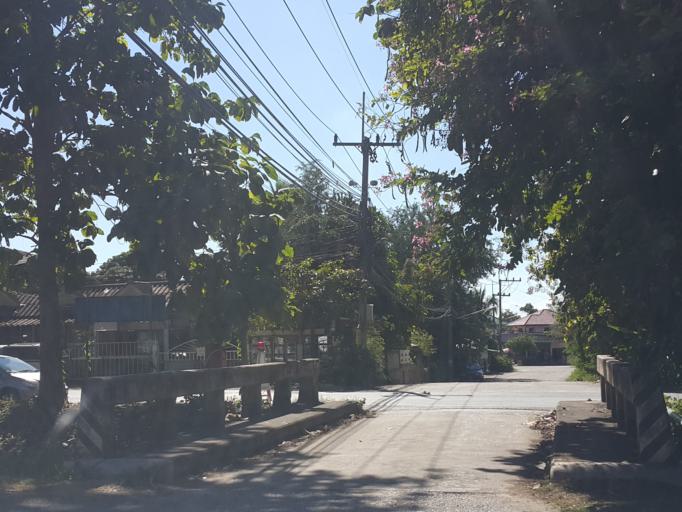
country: TH
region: Chiang Mai
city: San Sai
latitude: 18.8821
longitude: 99.1421
